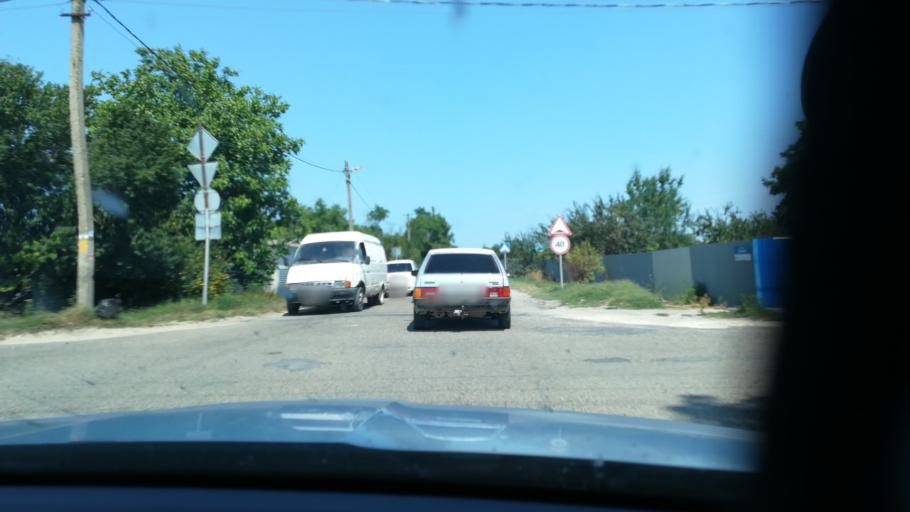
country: RU
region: Krasnodarskiy
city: Starotitarovskaya
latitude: 45.2059
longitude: 37.1468
